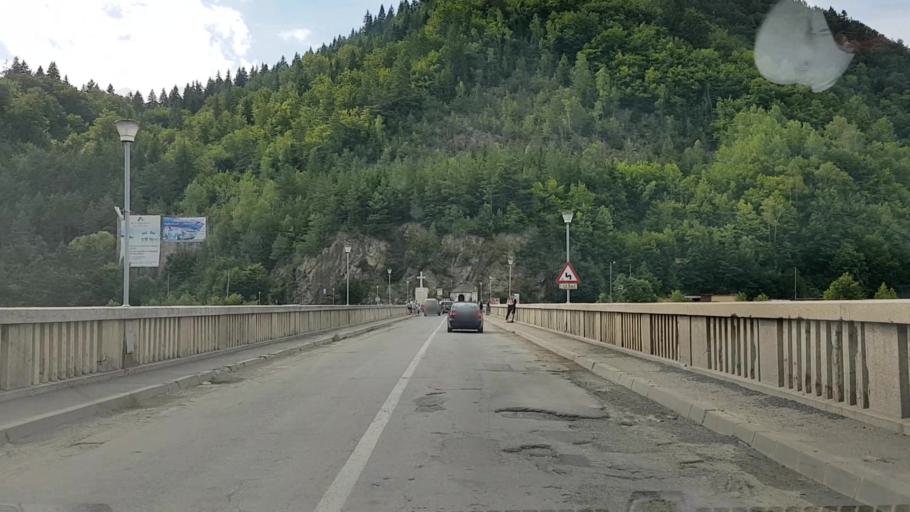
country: RO
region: Neamt
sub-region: Comuna Bicaz
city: Dodeni
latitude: 46.9388
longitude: 26.1024
